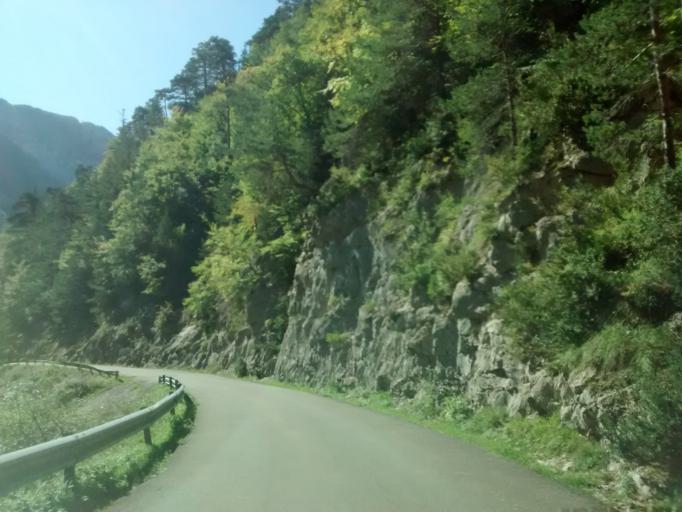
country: ES
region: Aragon
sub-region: Provincia de Huesca
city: Aragues del Puerto
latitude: 42.8198
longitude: -0.7119
